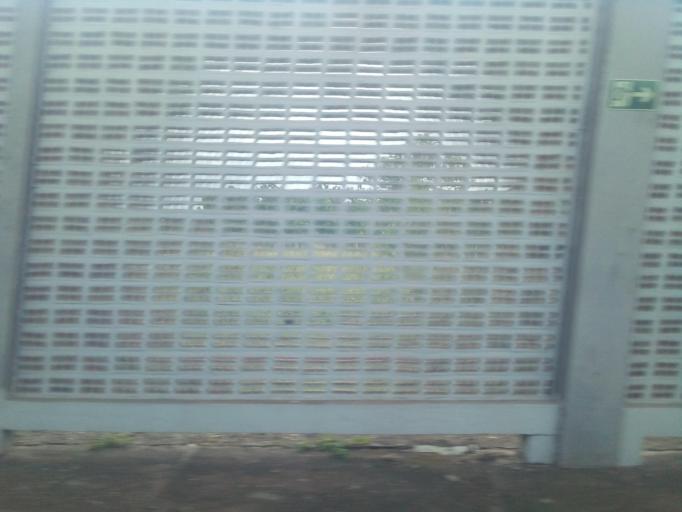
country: BR
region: Maranhao
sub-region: Santa Ines
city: Santa Ines
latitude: -3.6982
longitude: -45.4136
